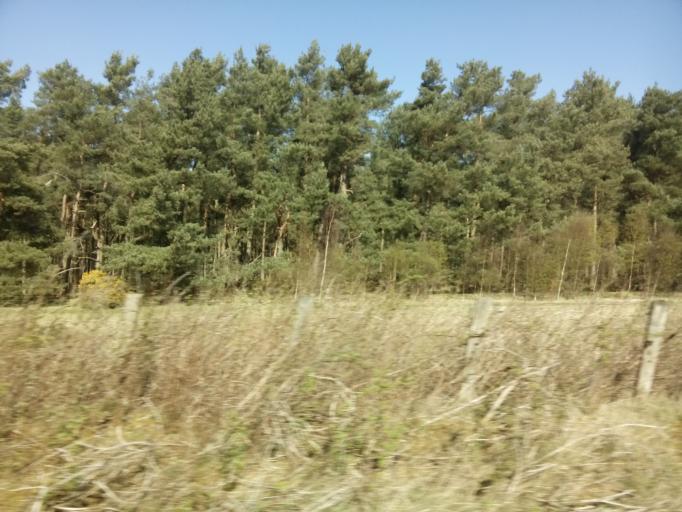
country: GB
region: Scotland
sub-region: Fife
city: Ladybank
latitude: 56.2812
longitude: -3.1151
